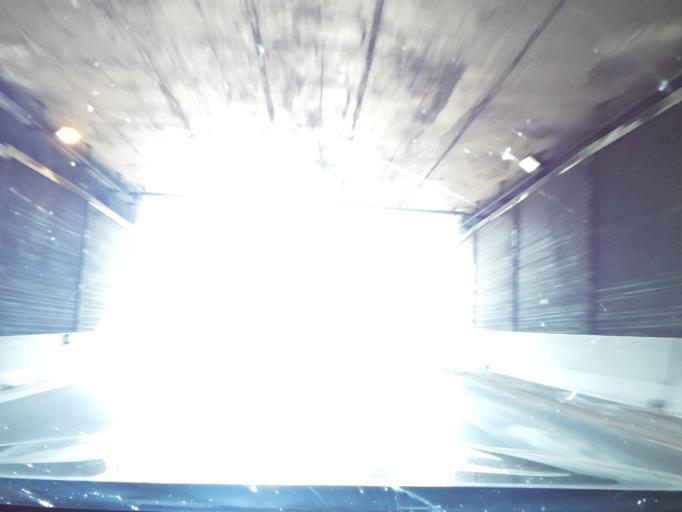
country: IT
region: Veneto
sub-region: Provincia di Verona
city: Verona
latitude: 45.4335
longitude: 10.9497
